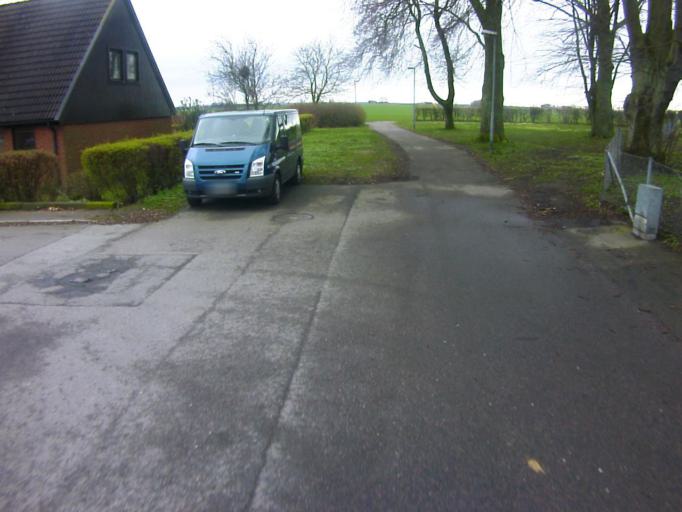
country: SE
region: Skane
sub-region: Kavlinge Kommun
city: Kaevlinge
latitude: 55.7724
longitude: 13.0961
